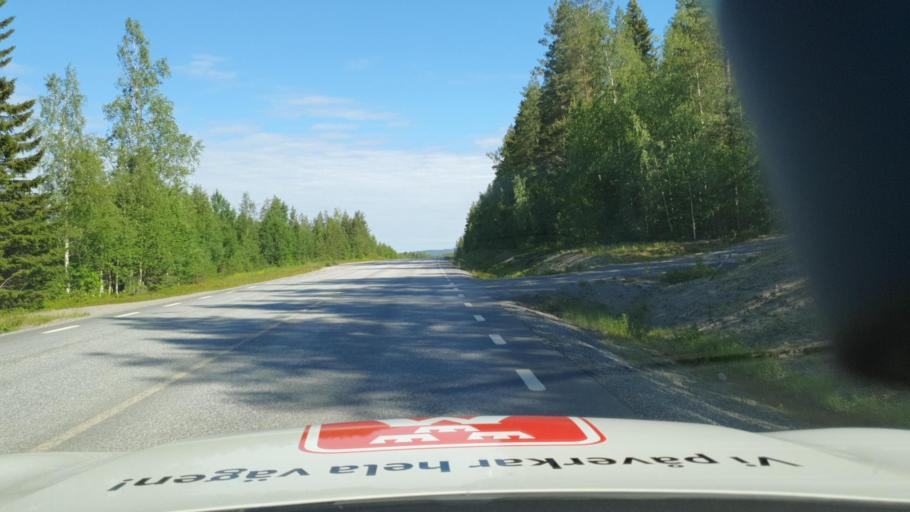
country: SE
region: Vaesterbotten
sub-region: Vannas Kommun
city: Vannasby
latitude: 64.0497
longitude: 19.9985
